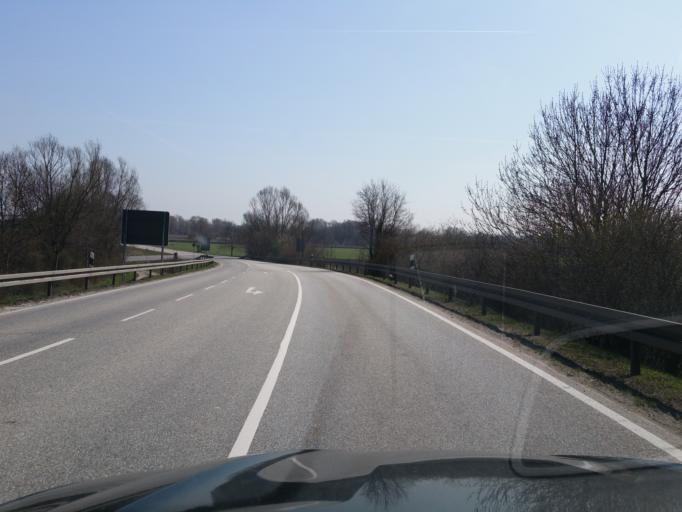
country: DE
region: Bavaria
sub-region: Upper Bavaria
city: Eitting
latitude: 48.3708
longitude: 11.8560
